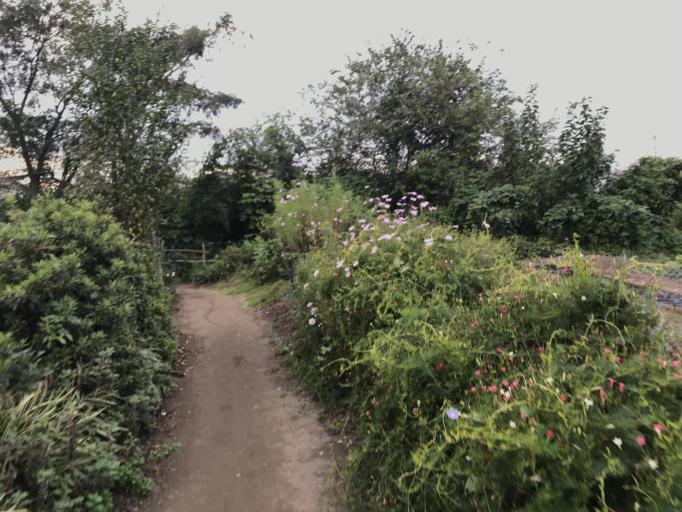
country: JP
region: Saitama
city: Hasuda
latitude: 35.9919
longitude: 139.6563
